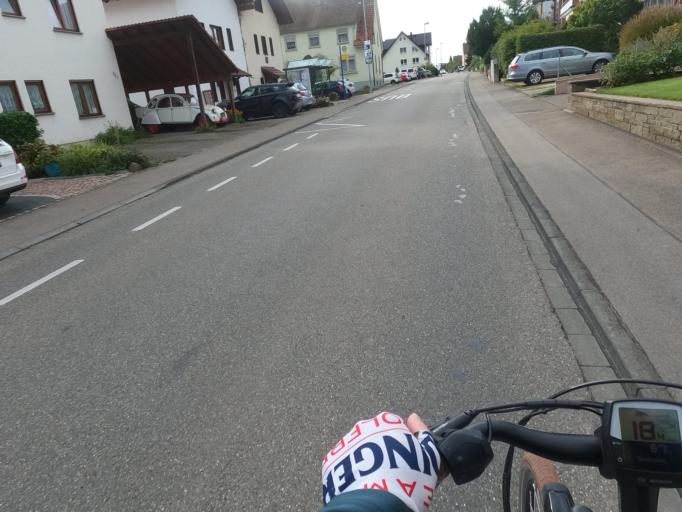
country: DE
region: Baden-Wuerttemberg
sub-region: Freiburg Region
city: Allensbach
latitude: 47.7194
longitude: 9.0574
